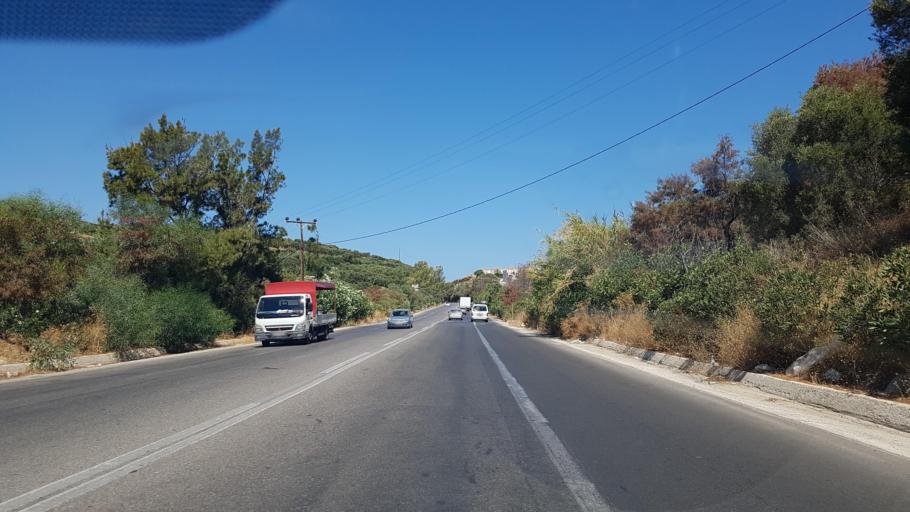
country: GR
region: Crete
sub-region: Nomos Chanias
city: Agia Marina
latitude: 35.5114
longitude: 23.9298
